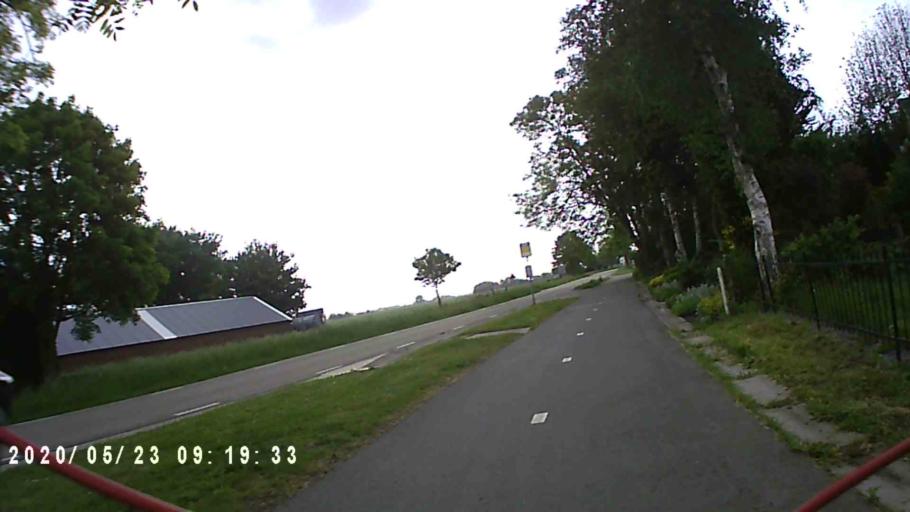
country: NL
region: Groningen
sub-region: Gemeente Bedum
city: Bedum
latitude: 53.2977
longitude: 6.6678
